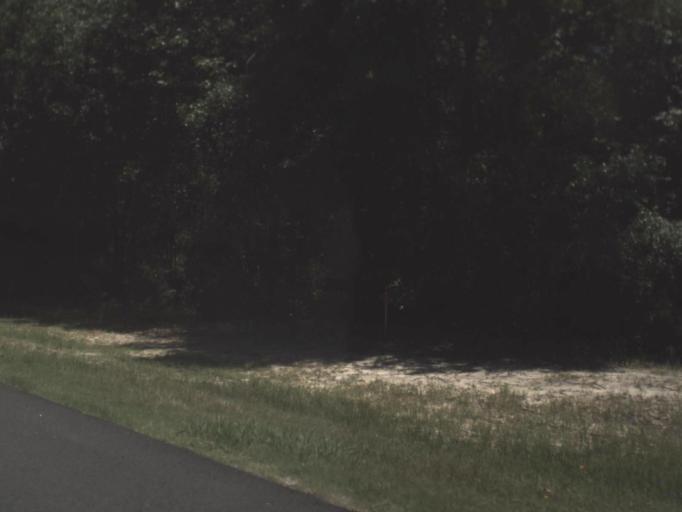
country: US
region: Florida
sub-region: Suwannee County
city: Wellborn
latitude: 30.1951
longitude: -82.7569
